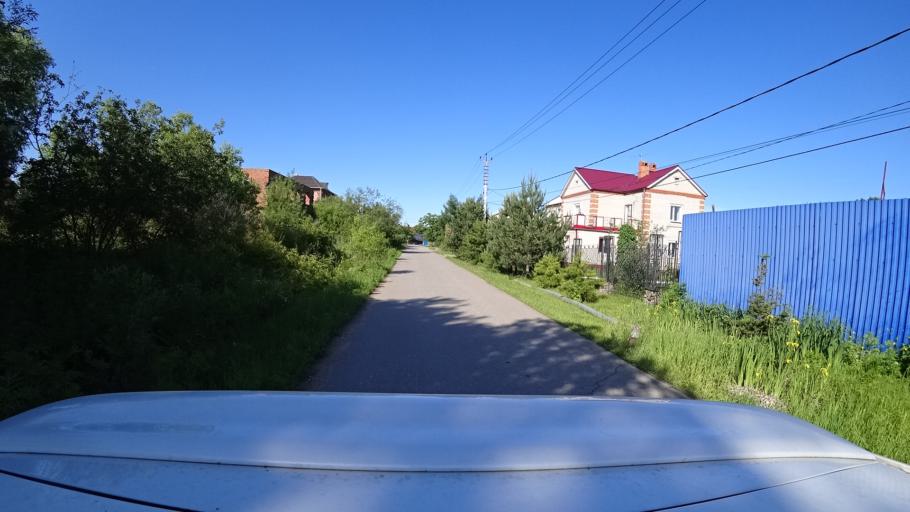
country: RU
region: Khabarovsk Krai
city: Topolevo
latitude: 48.5445
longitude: 135.1789
